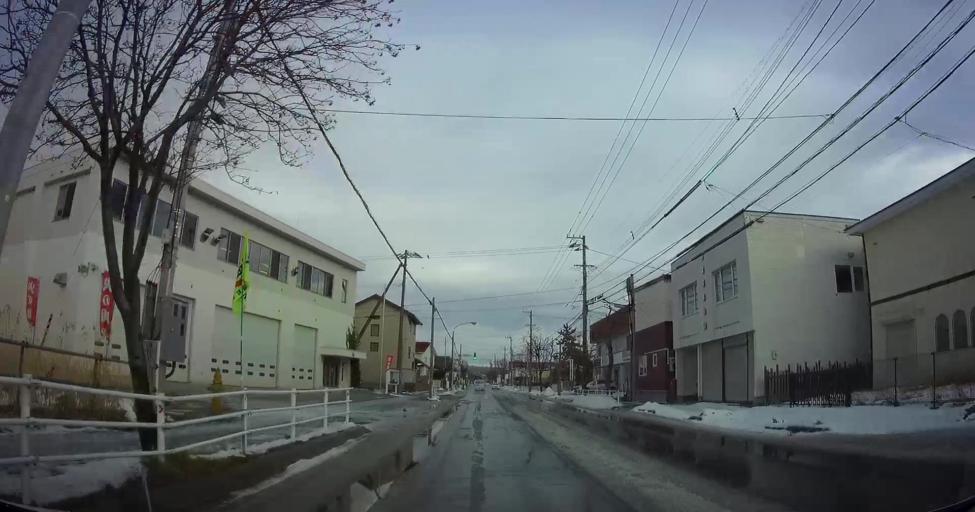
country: JP
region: Hokkaido
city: Hakodate
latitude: 41.7786
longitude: 140.7556
